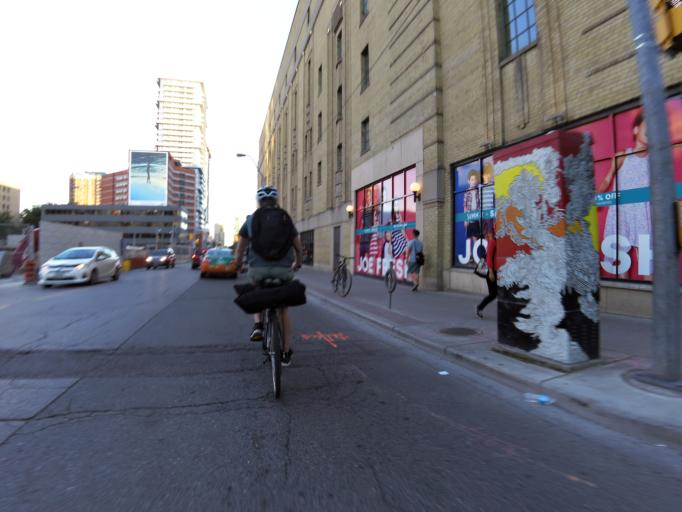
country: CA
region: Ontario
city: Toronto
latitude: 43.6627
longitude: -79.3798
